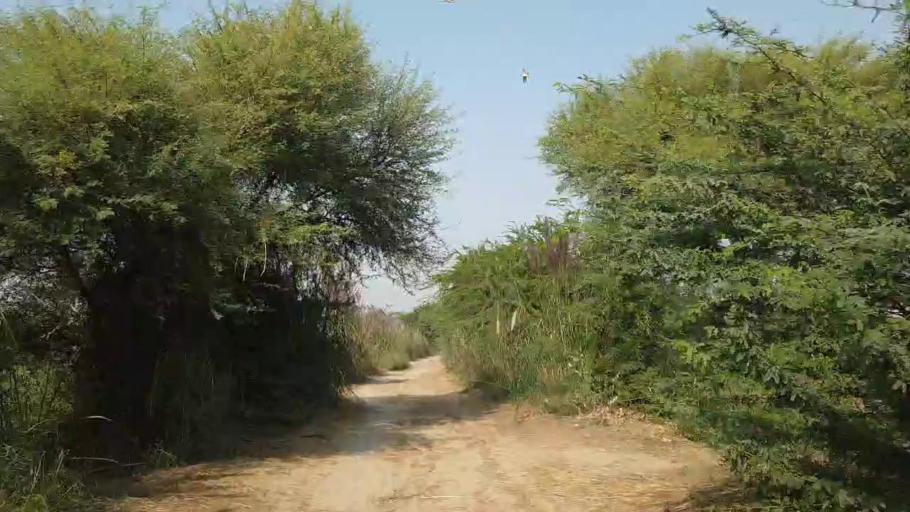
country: PK
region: Sindh
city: Matli
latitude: 24.9503
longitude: 68.5564
